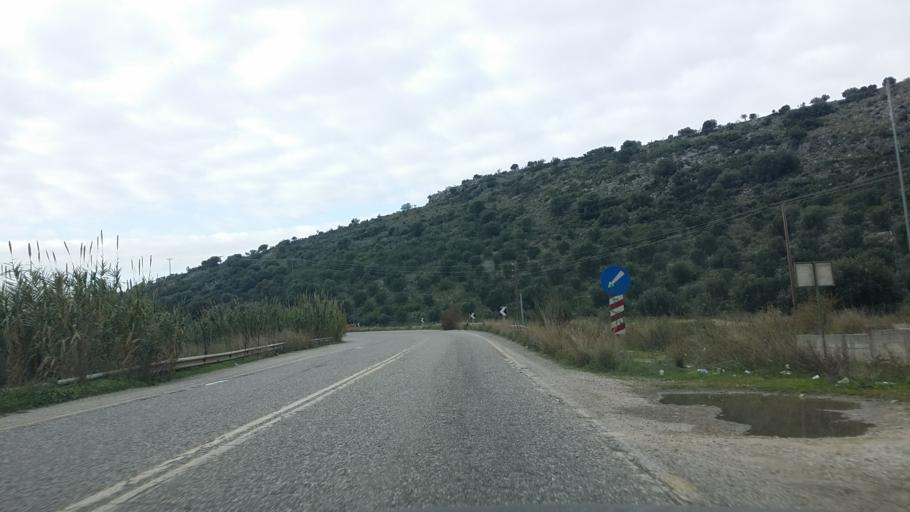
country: GR
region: West Greece
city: Aitoliko
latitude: 38.4122
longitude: 21.3964
